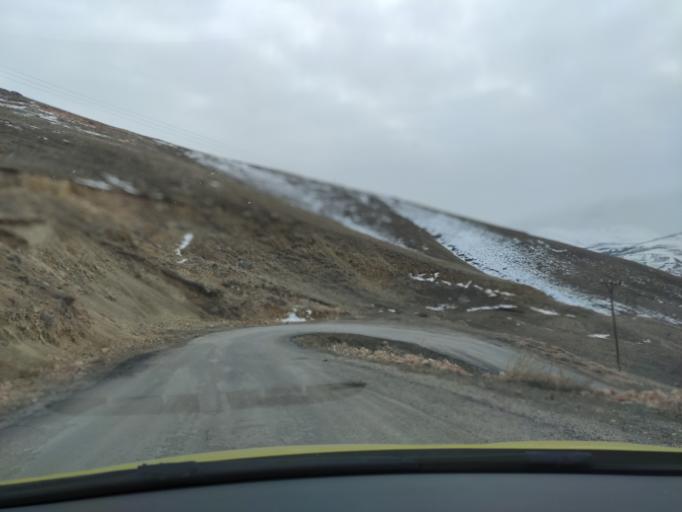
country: TR
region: Bayburt
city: Bayburt
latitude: 40.2579
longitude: 40.2412
